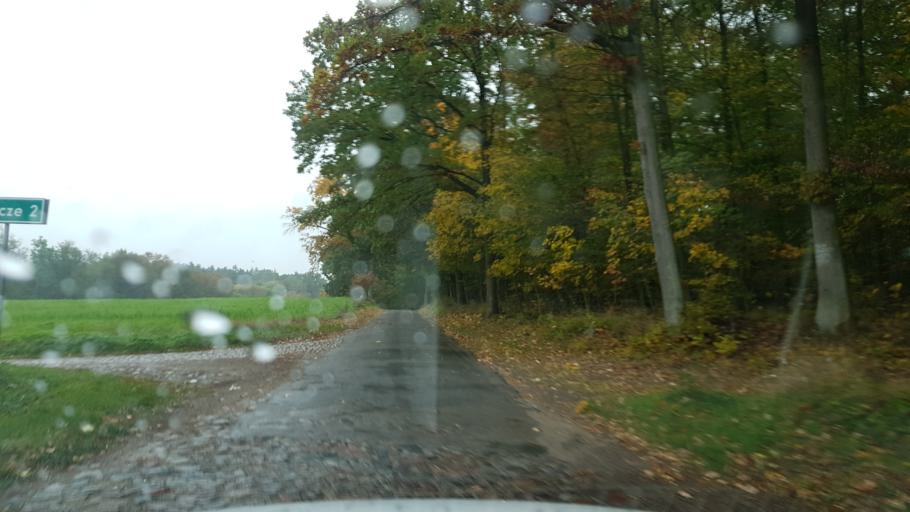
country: PL
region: West Pomeranian Voivodeship
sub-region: Powiat mysliborski
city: Barlinek
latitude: 53.0290
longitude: 15.2294
